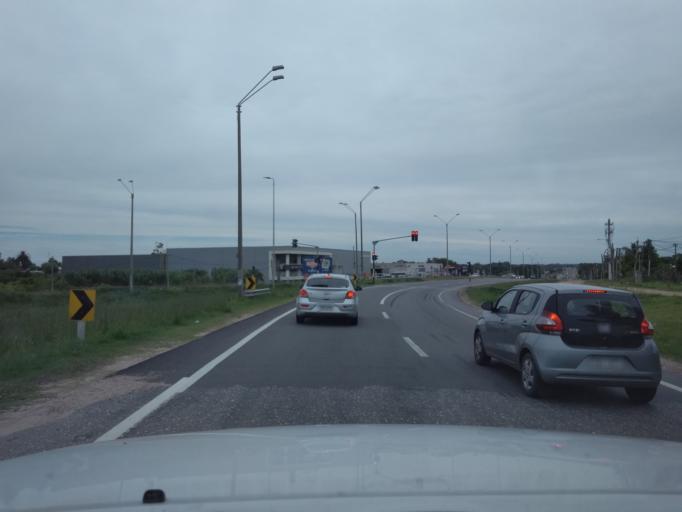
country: UY
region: Canelones
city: Colonia Nicolich
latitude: -34.8192
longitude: -56.0096
